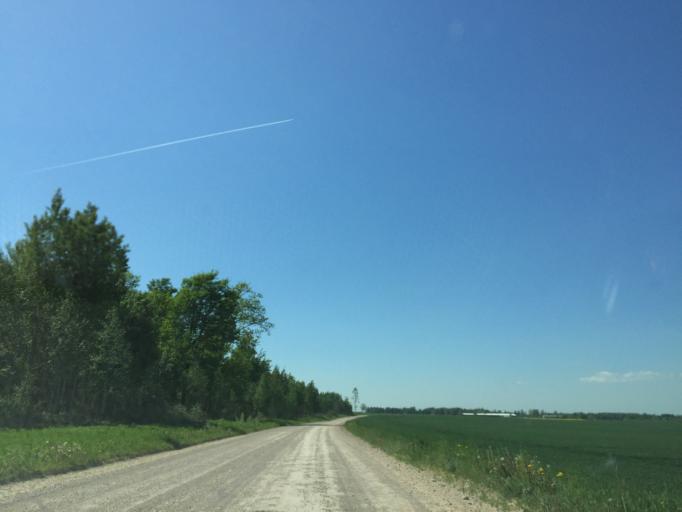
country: LV
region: Bauskas Rajons
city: Bauska
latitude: 56.4883
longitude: 24.1000
